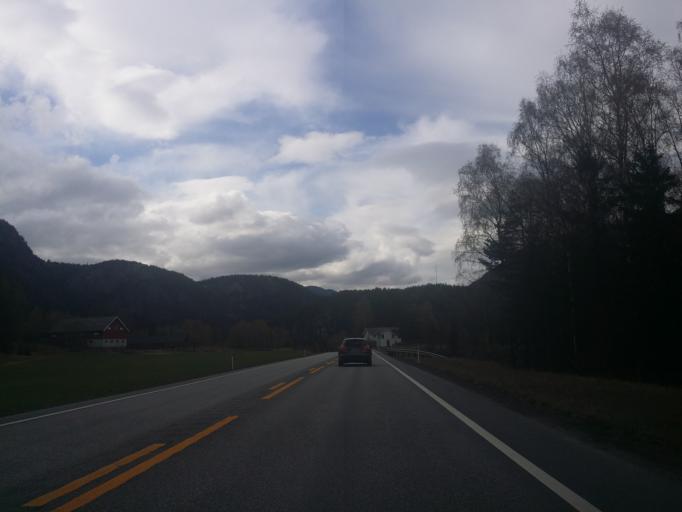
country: NO
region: Buskerud
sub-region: Nes
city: Nesbyen
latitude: 60.4661
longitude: 9.2486
